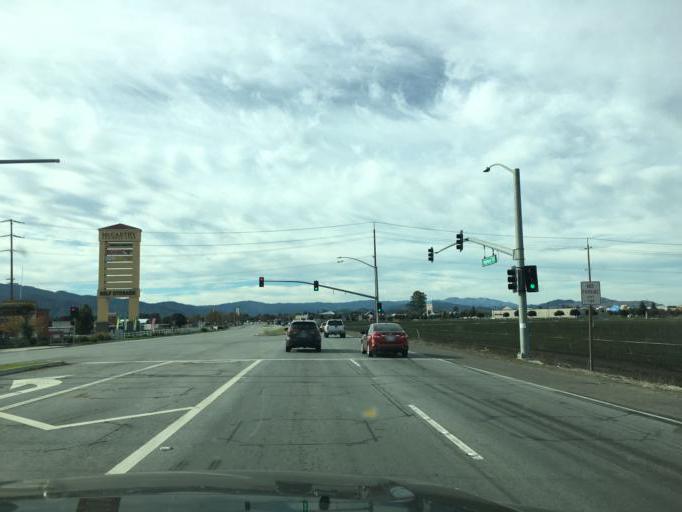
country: US
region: California
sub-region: Santa Clara County
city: Gilroy
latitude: 37.0037
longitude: -121.5442
